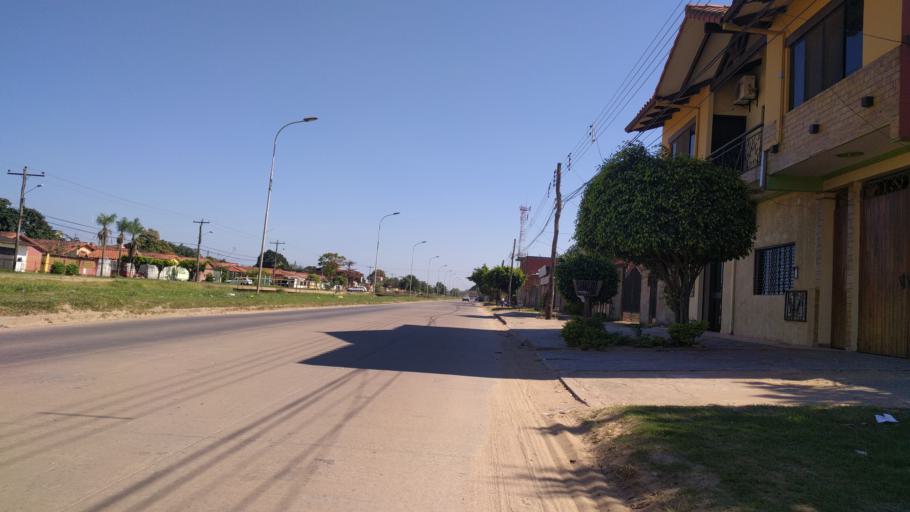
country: BO
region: Santa Cruz
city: Santa Cruz de la Sierra
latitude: -17.8559
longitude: -63.1914
